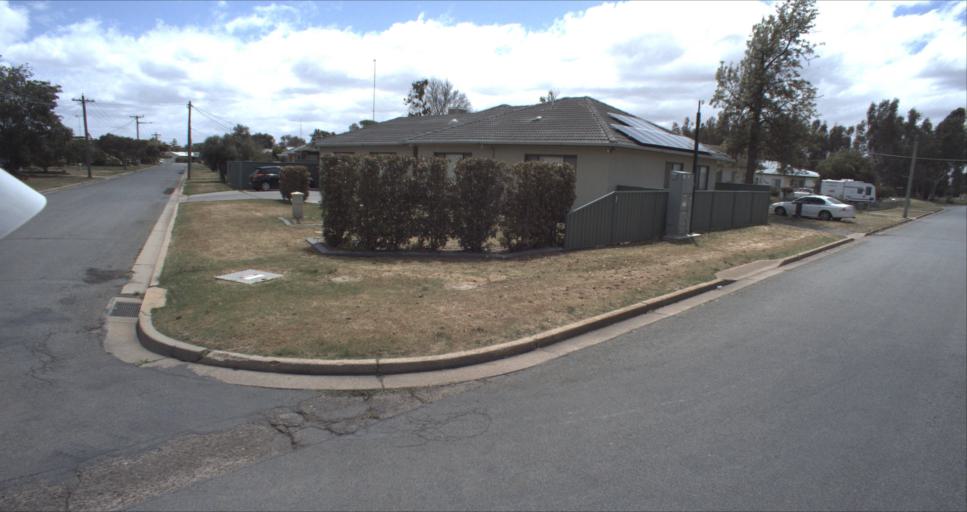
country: AU
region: New South Wales
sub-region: Leeton
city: Leeton
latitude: -34.5568
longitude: 146.3910
